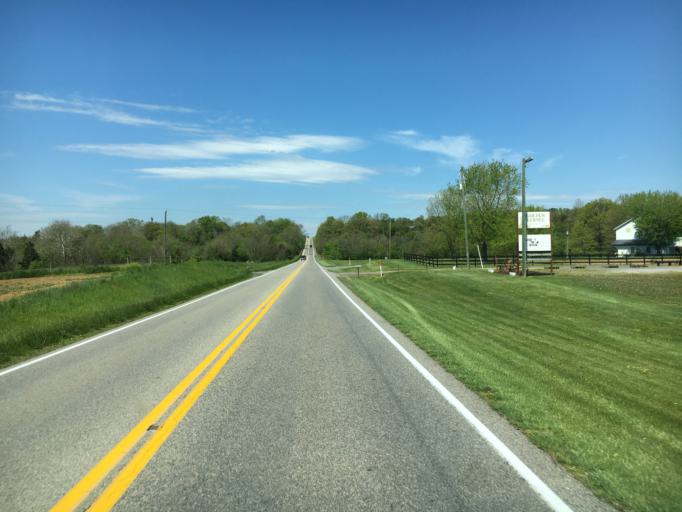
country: US
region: Virginia
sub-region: Rockingham County
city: Grottoes
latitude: 38.2672
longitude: -78.8618
